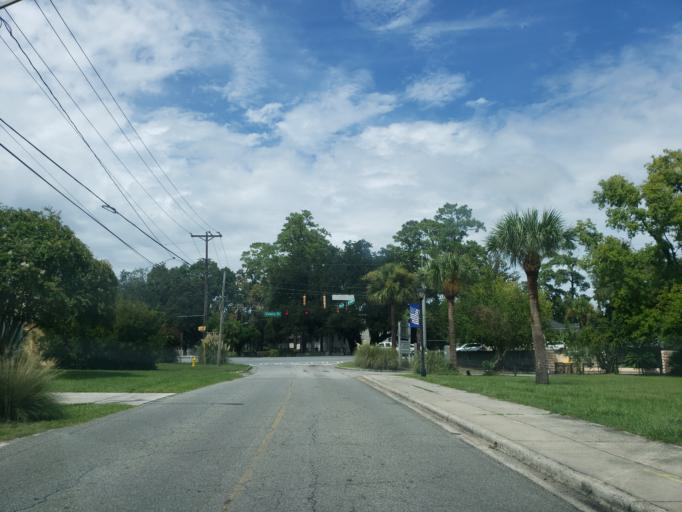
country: US
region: Georgia
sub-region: Chatham County
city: Thunderbolt
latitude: 32.0335
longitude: -81.0500
